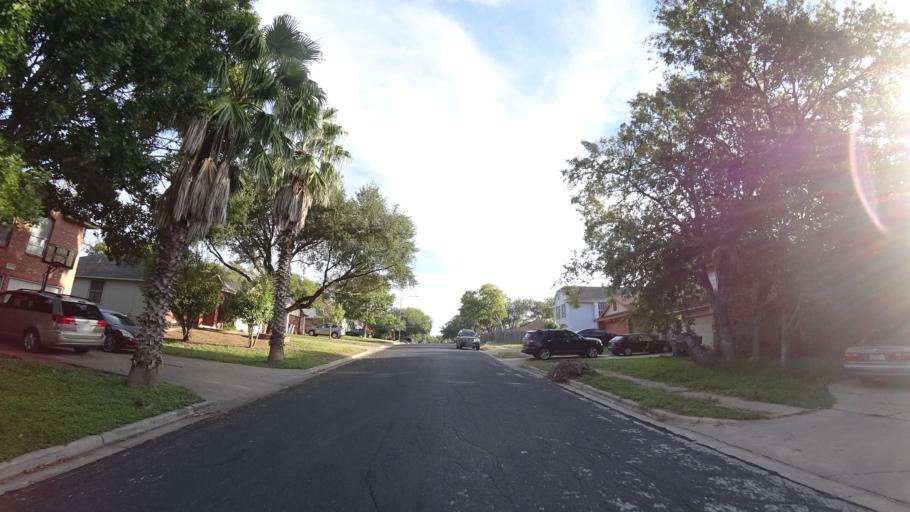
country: US
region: Texas
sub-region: Travis County
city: Onion Creek
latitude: 30.1910
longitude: -97.7383
